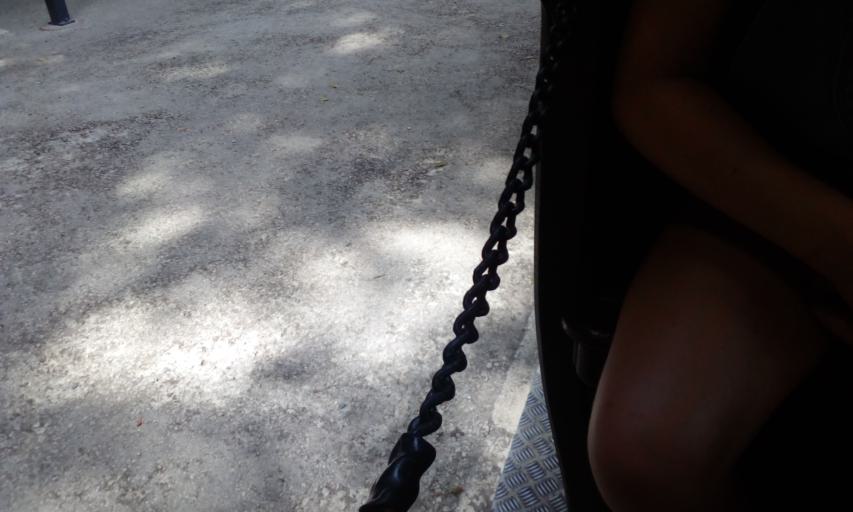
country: BE
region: Wallonia
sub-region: Province du Luxembourg
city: Tellin
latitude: 50.1184
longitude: 5.1991
